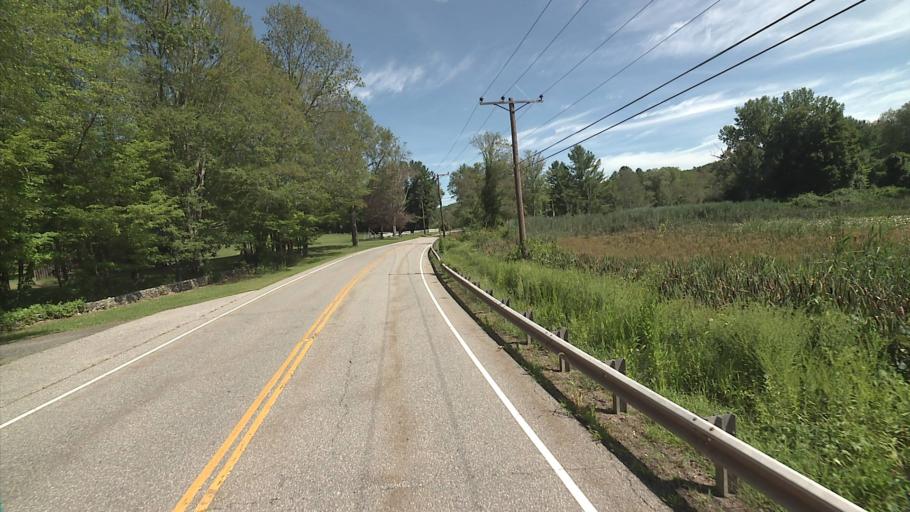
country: US
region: Connecticut
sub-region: New London County
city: Baltic
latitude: 41.6725
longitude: -72.0857
